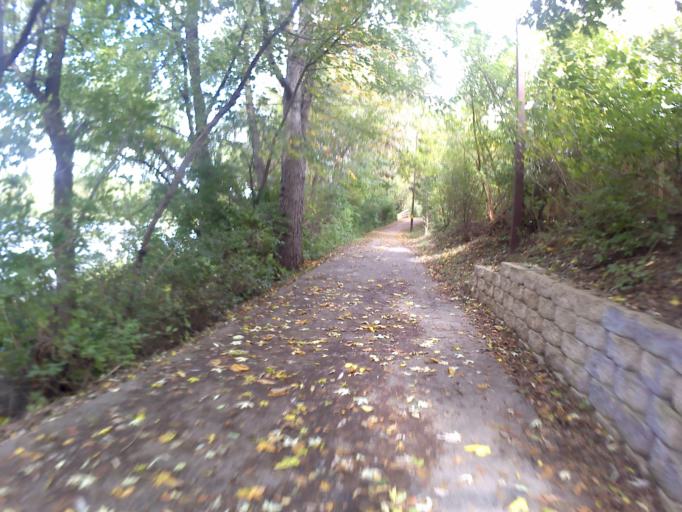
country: US
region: Illinois
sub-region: Kane County
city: Batavia
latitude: 41.8362
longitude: -88.3086
